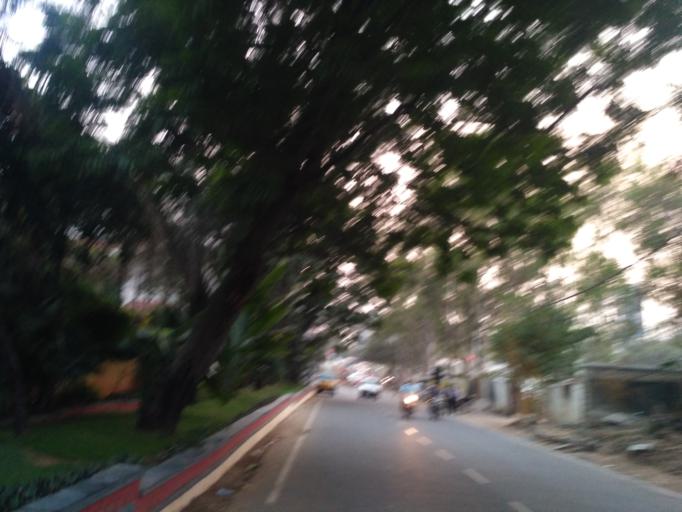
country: IN
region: Telangana
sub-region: Rangareddi
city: Kukatpalli
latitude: 17.4394
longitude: 78.4003
